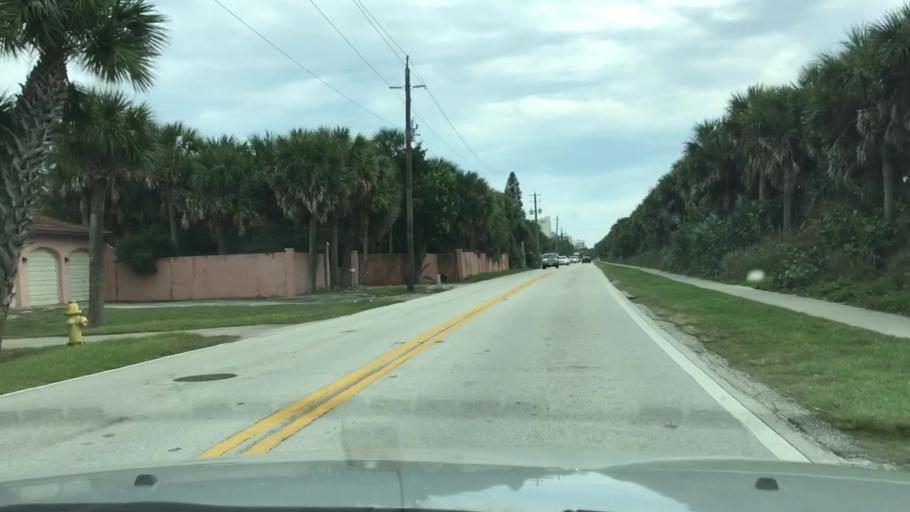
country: US
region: Florida
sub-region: Volusia County
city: Ormond Beach
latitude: 29.2983
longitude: -81.0430
